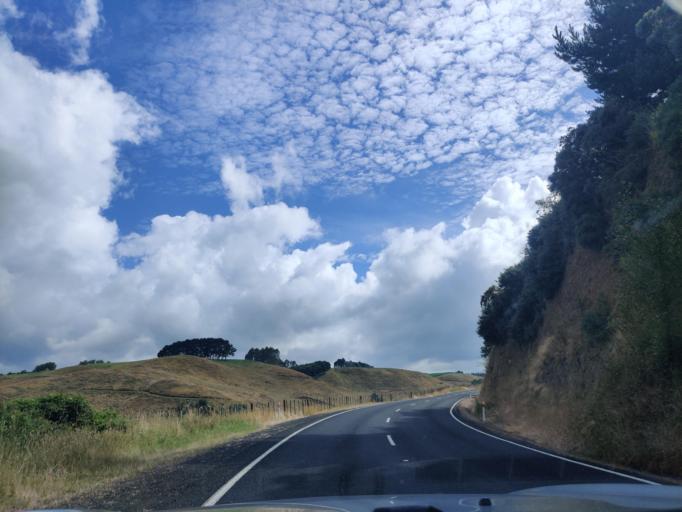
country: NZ
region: Waikato
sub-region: Otorohanga District
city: Otorohanga
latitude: -38.0954
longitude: 175.1442
